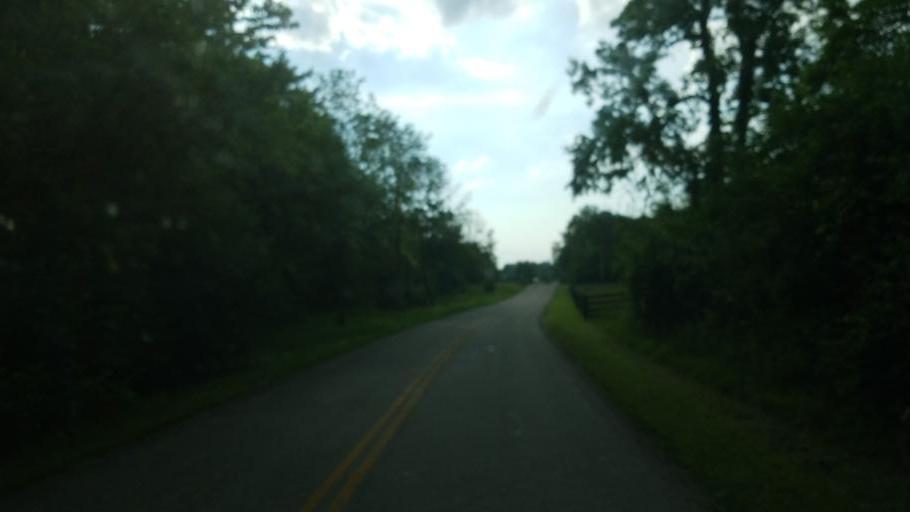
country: US
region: Ohio
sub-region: Knox County
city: Centerburg
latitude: 40.3215
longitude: -82.7683
